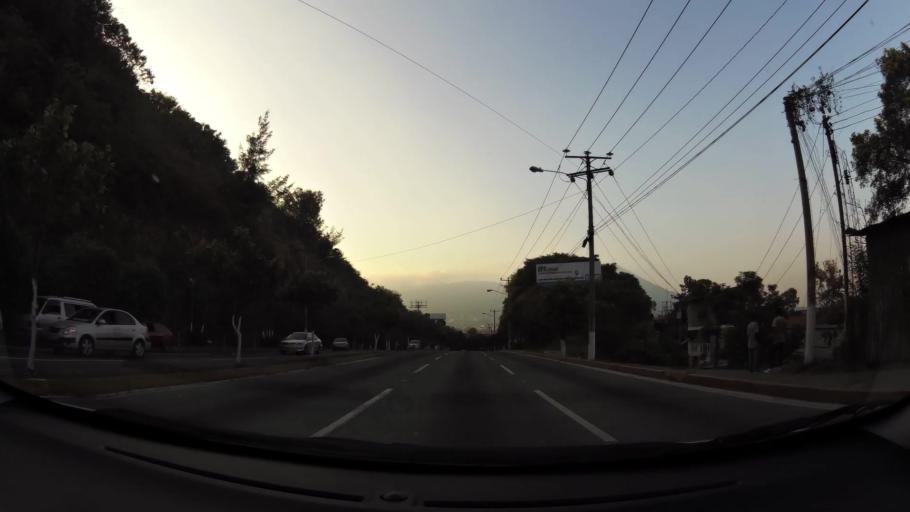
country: SV
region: San Salvador
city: San Salvador
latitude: 13.6817
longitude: -89.2160
